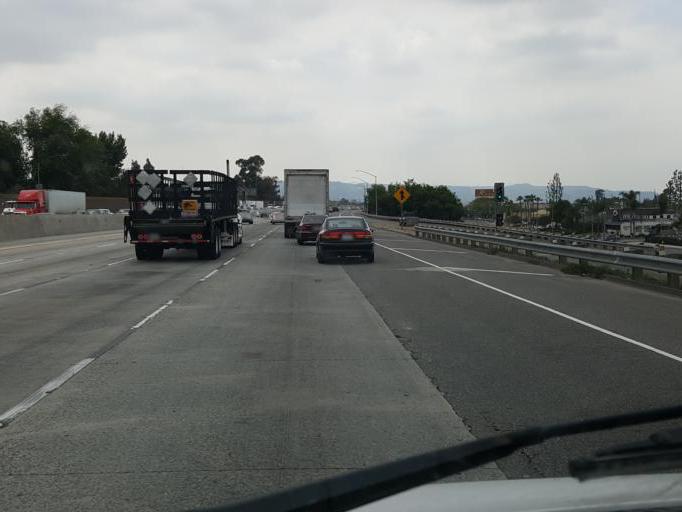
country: US
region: California
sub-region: Los Angeles County
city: Rowland Heights
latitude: 33.9943
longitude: -117.9066
